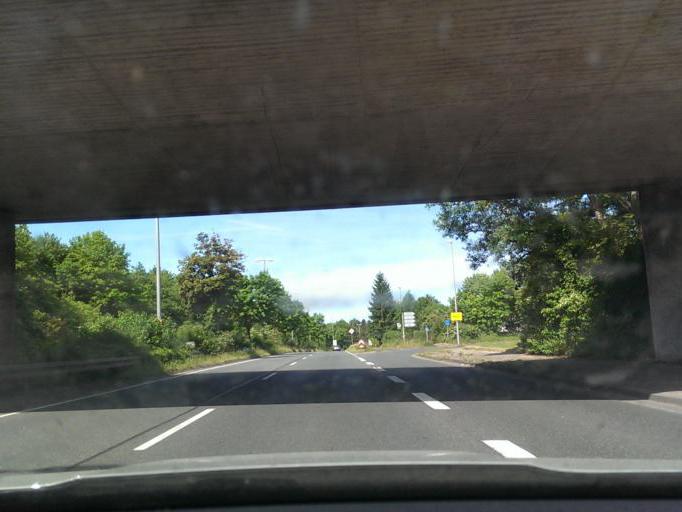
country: DE
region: Lower Saxony
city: Hildesheim
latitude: 52.1570
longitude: 9.9146
